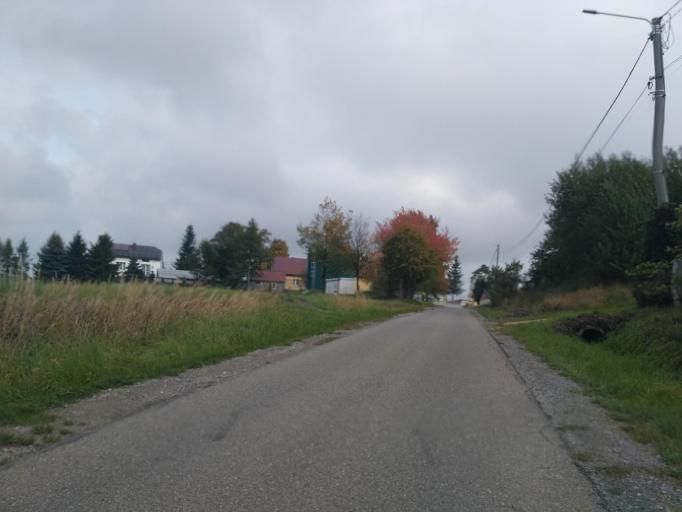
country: PL
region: Subcarpathian Voivodeship
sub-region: Powiat ropczycko-sedziszowski
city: Niedzwiada
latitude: 49.9630
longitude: 21.4440
